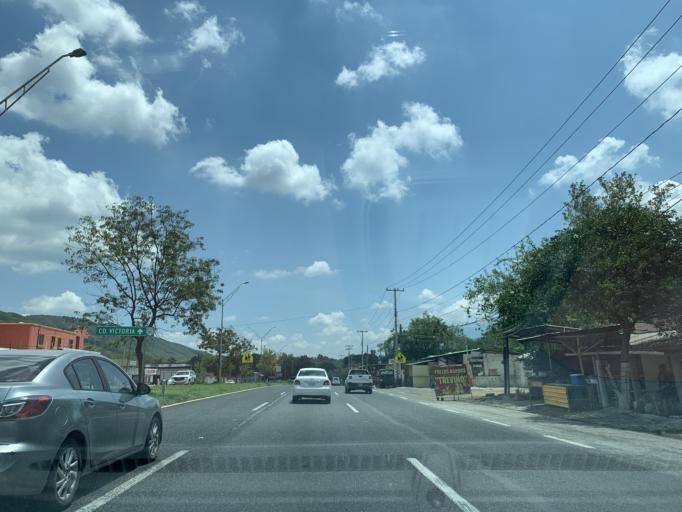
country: MX
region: Nuevo Leon
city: Santiago
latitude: 25.3838
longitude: -100.1148
